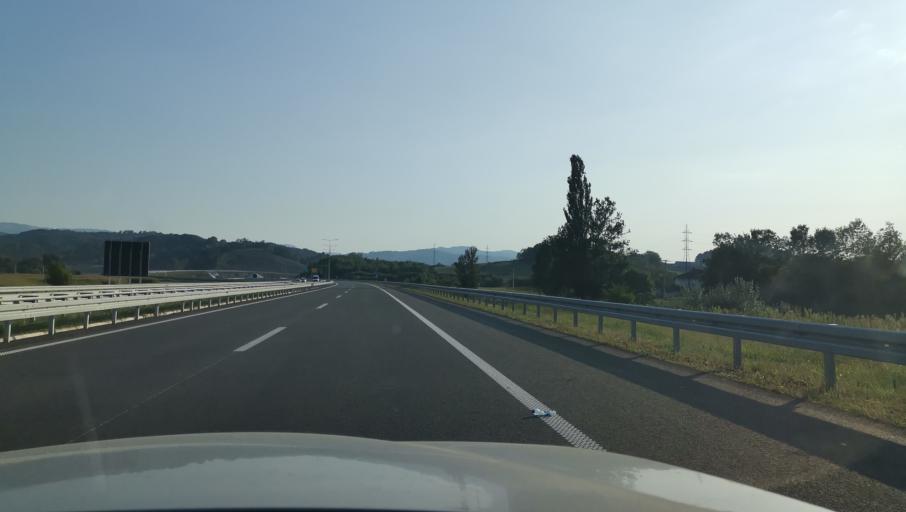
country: RS
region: Central Serbia
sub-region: Kolubarski Okrug
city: Ljig
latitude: 44.2390
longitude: 20.2593
